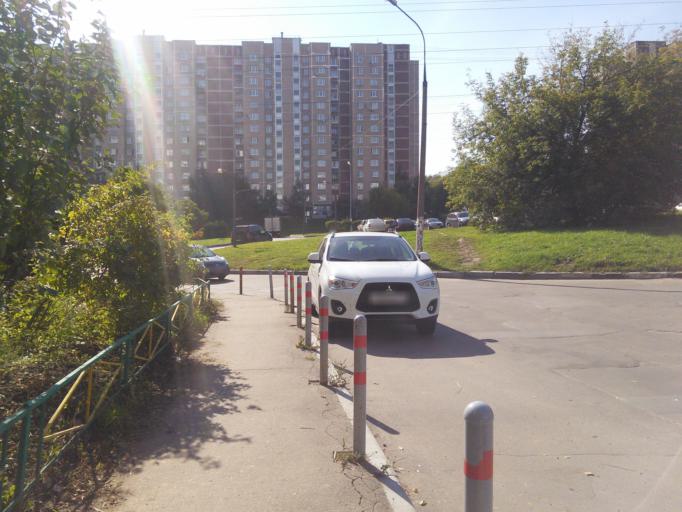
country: RU
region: Moscow
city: Orekhovo-Borisovo Severnoye
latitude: 55.6376
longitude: 37.6784
